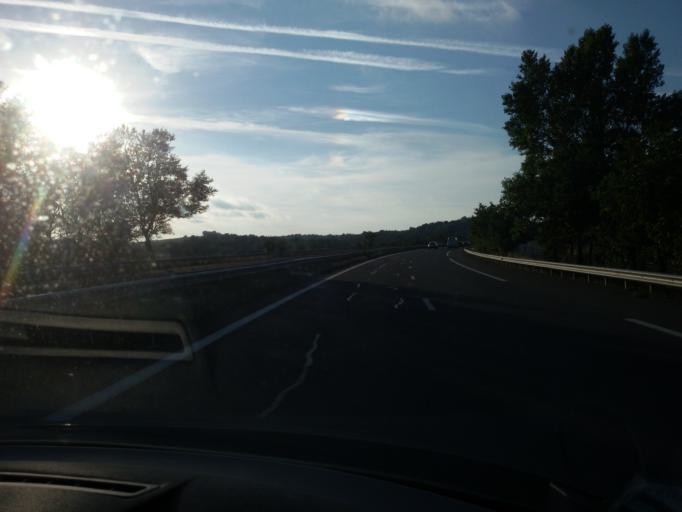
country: FR
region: Languedoc-Roussillon
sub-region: Departement de l'Herault
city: Lodeve
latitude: 43.8896
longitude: 3.2868
